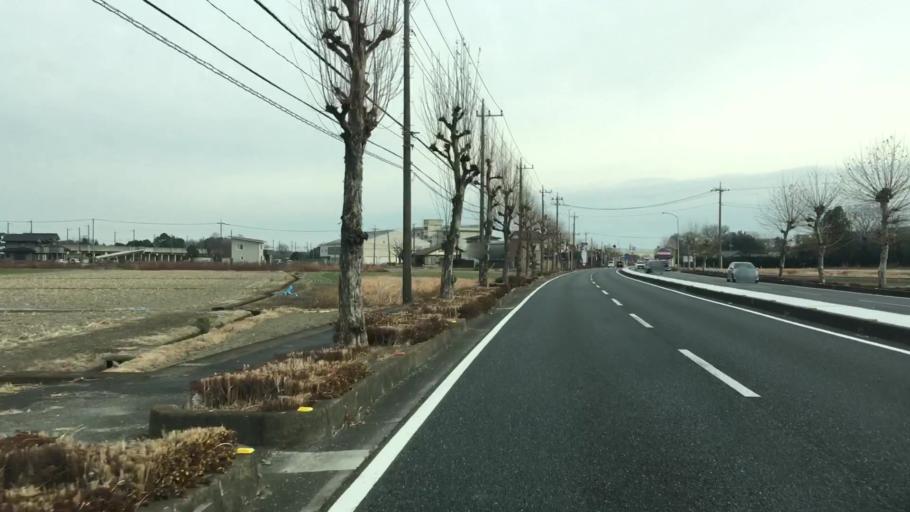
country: JP
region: Saitama
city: Kumagaya
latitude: 36.1508
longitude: 139.3363
